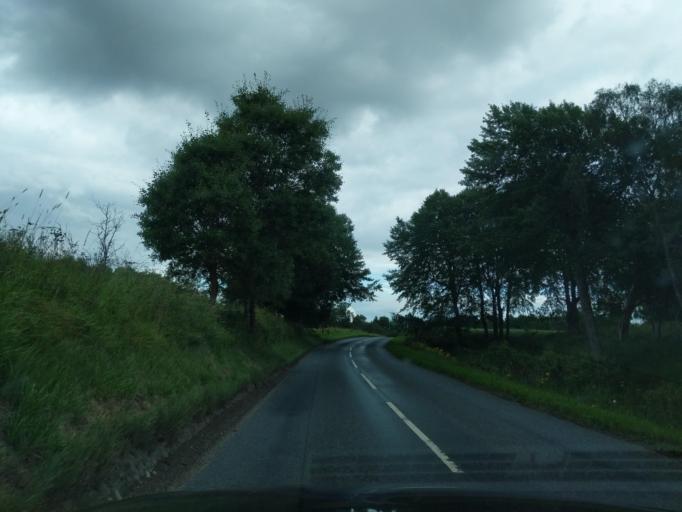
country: GB
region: Scotland
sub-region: Highland
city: Aviemore
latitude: 57.2870
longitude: -3.8060
